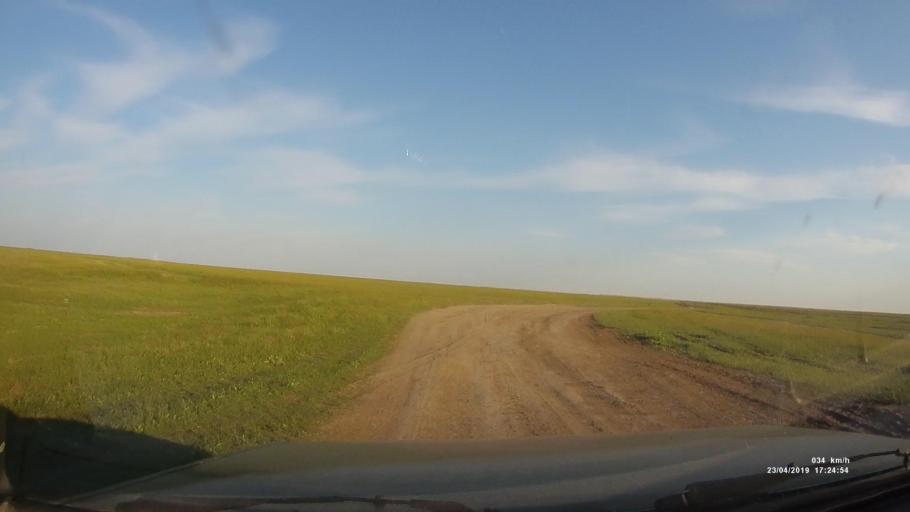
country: RU
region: Kalmykiya
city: Priyutnoye
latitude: 46.1551
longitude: 43.5093
